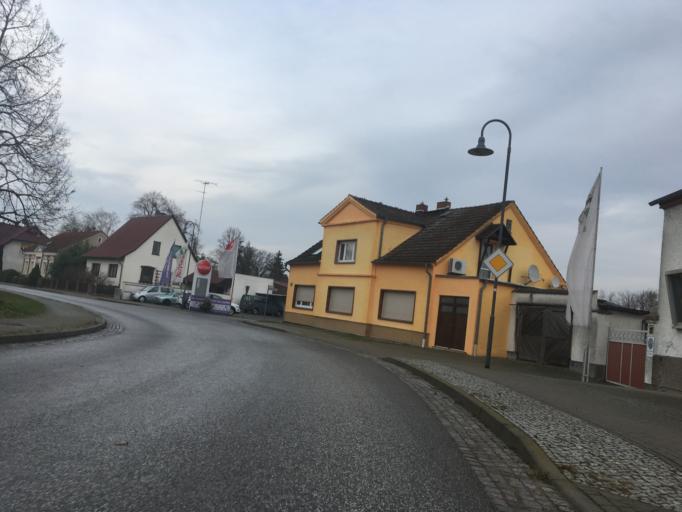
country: DE
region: Brandenburg
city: Letschin
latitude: 52.6401
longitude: 14.3607
